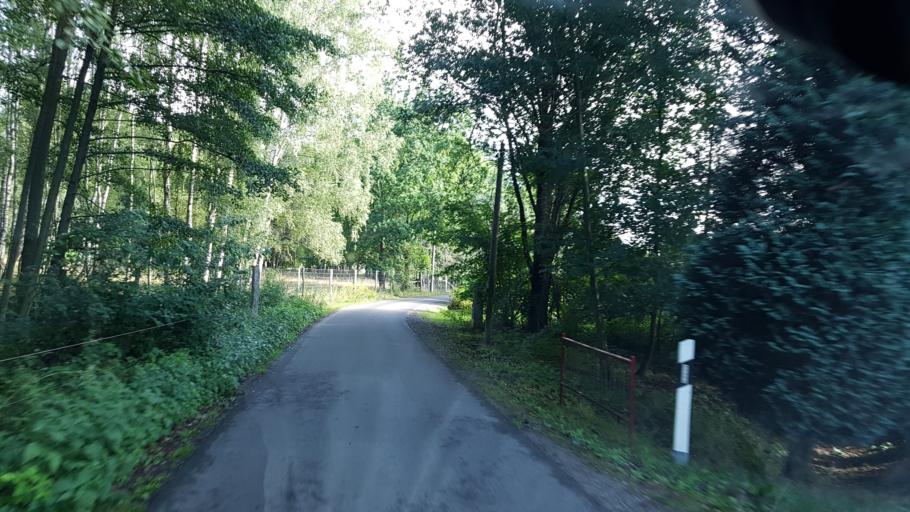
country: DE
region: Brandenburg
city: Tschernitz
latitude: 51.6278
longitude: 14.5843
